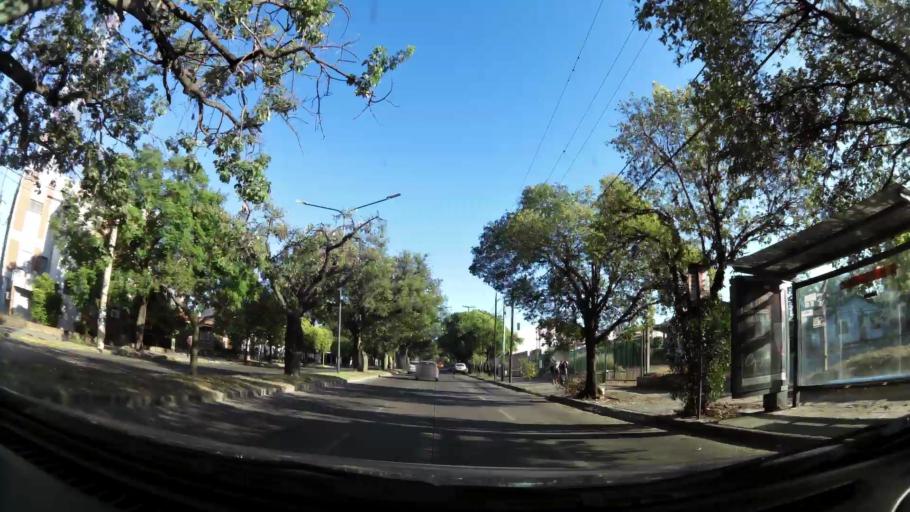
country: AR
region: Cordoba
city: Villa Allende
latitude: -31.3478
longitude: -64.2496
